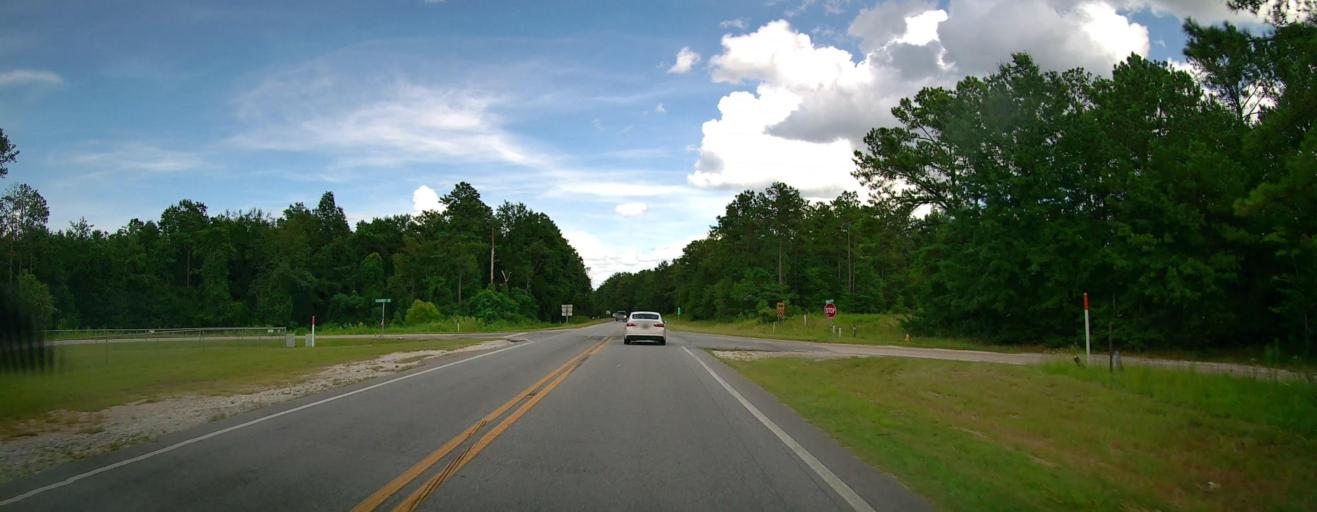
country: US
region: Alabama
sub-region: Russell County
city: Ladonia
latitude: 32.4507
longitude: -85.2216
